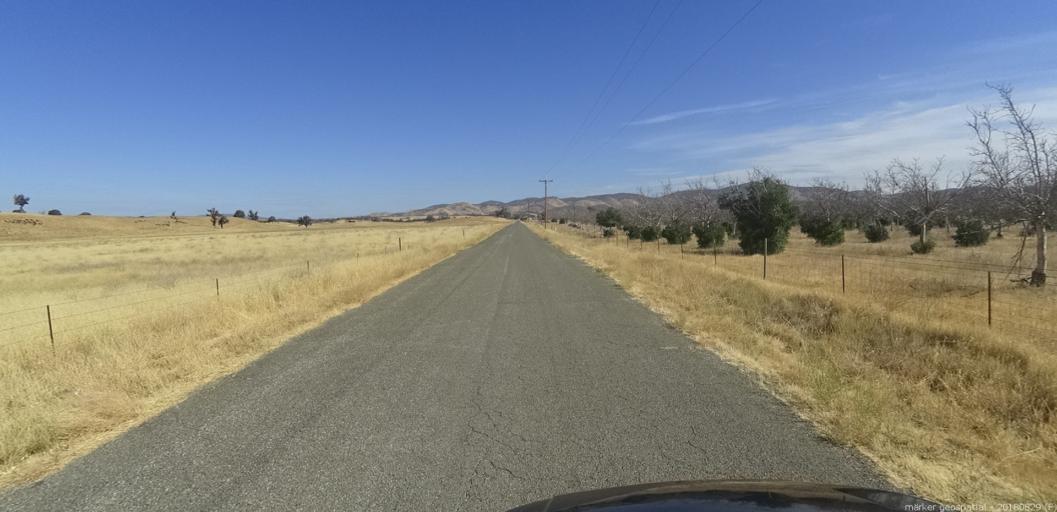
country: US
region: California
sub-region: Monterey County
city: King City
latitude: 35.9519
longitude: -121.1176
